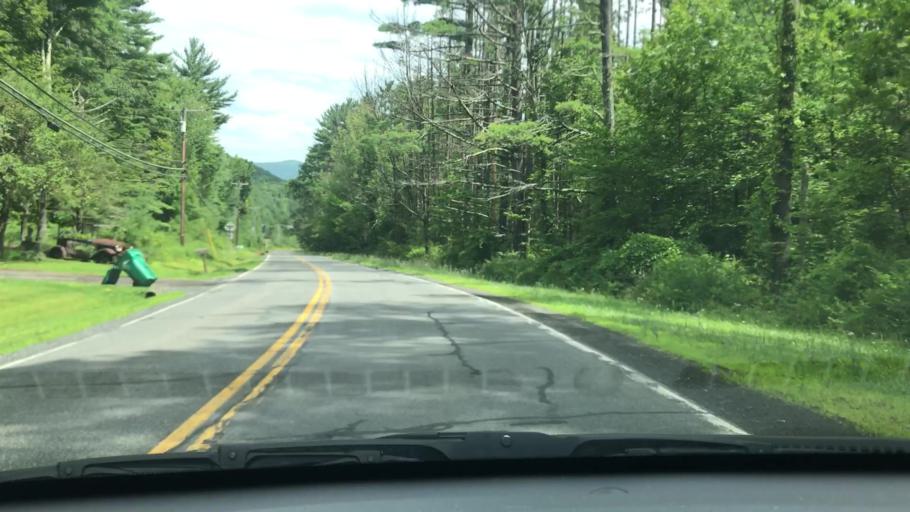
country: US
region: New York
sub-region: Ulster County
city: Shokan
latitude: 41.9943
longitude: -74.2780
